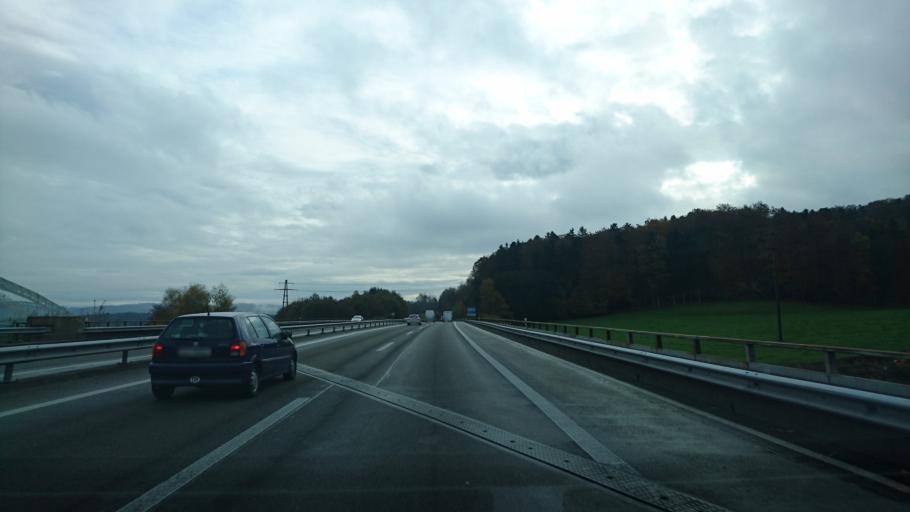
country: CH
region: Aargau
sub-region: Bezirk Zofingen
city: Safenwil
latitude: 47.3231
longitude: 8.0052
